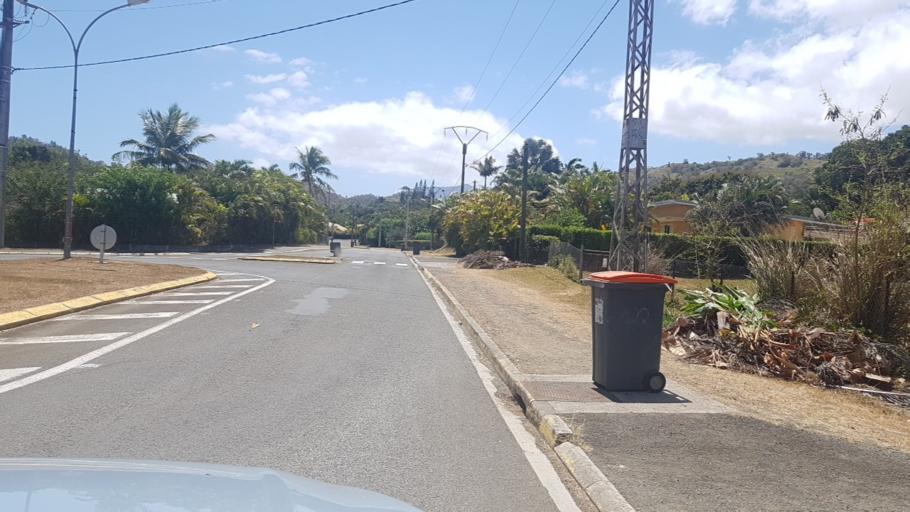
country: NC
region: South Province
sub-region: Dumbea
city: Dumbea
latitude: -22.1373
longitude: 166.4345
